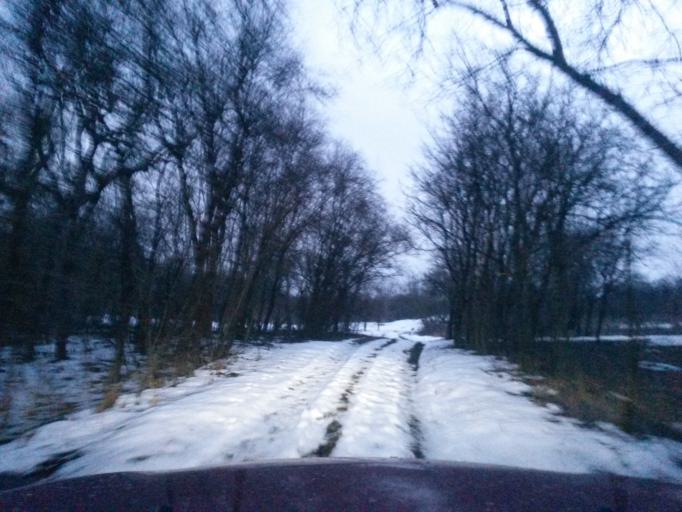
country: SK
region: Kosicky
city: Secovce
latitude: 48.7139
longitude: 21.6285
